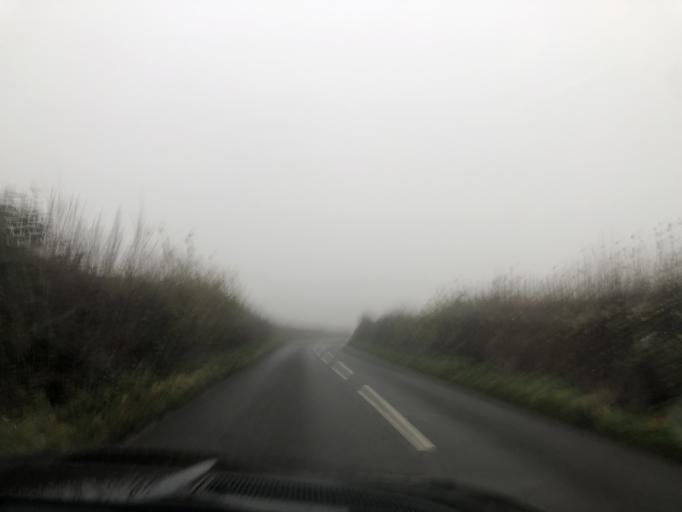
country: GB
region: England
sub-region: Oxfordshire
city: Bicester
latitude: 51.9200
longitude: -1.1816
